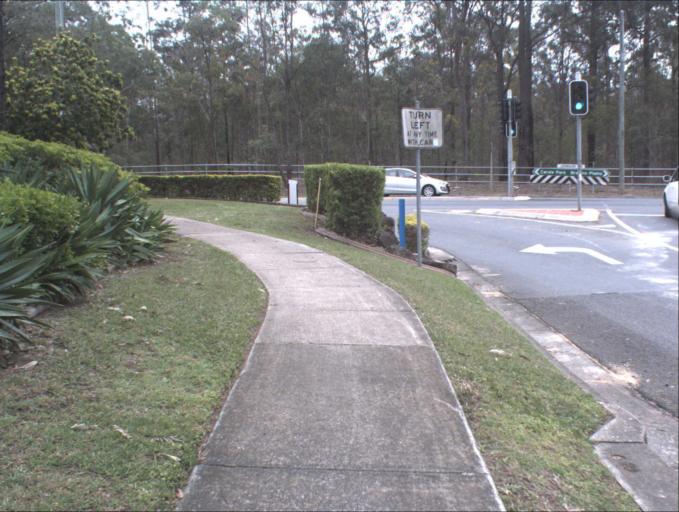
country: AU
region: Queensland
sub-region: Brisbane
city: Forest Lake
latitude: -27.6567
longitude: 153.0073
